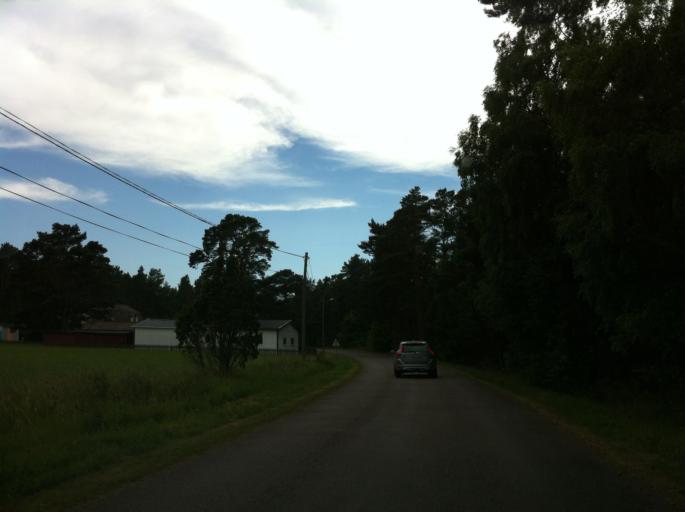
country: SE
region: Kalmar
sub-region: Vasterviks Kommun
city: Vaestervik
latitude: 57.3644
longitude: 17.0682
